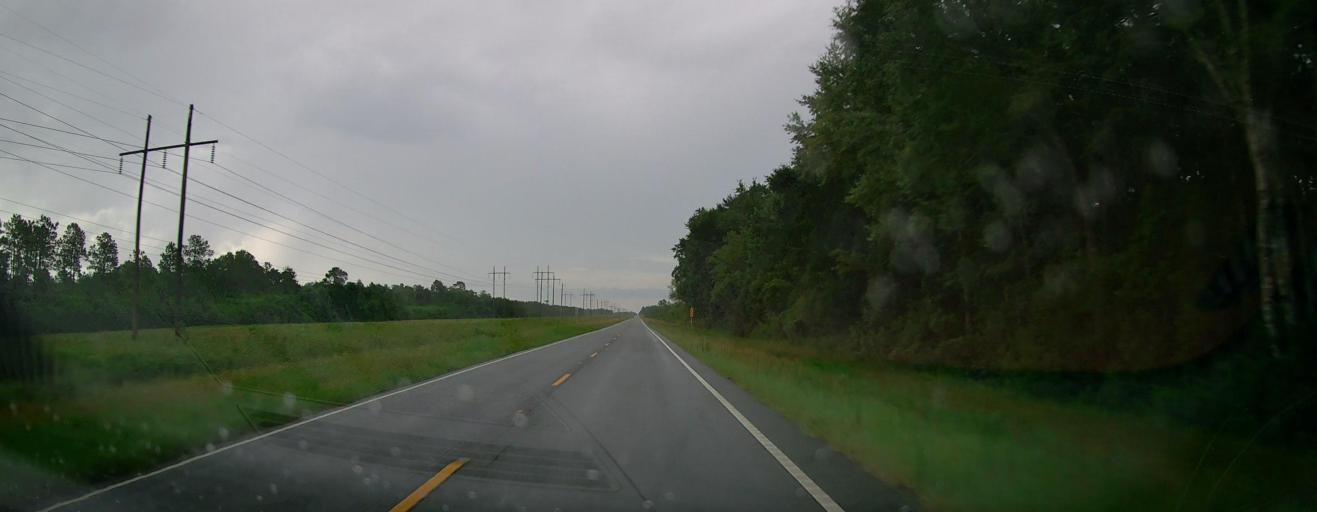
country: US
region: Georgia
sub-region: Brantley County
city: Nahunta
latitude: 31.3358
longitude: -81.8794
